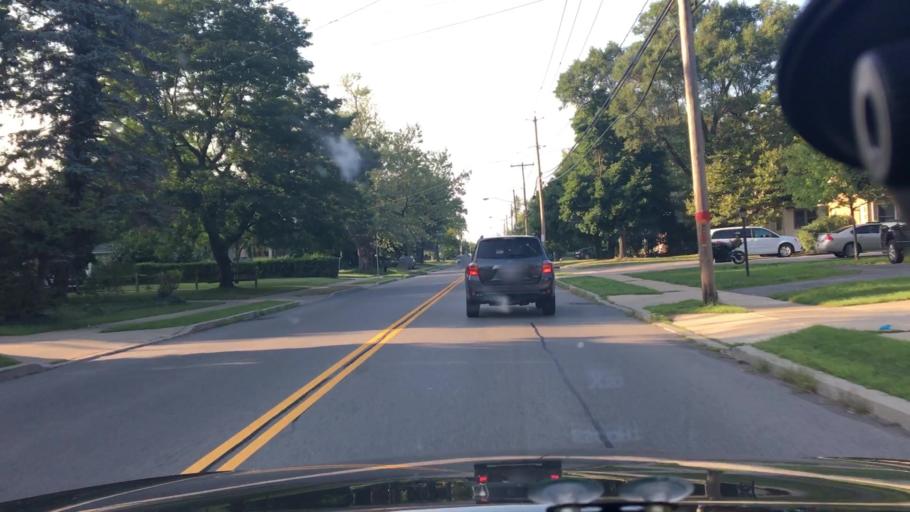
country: US
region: New York
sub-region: Erie County
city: Amherst
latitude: 42.9724
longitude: -78.7839
